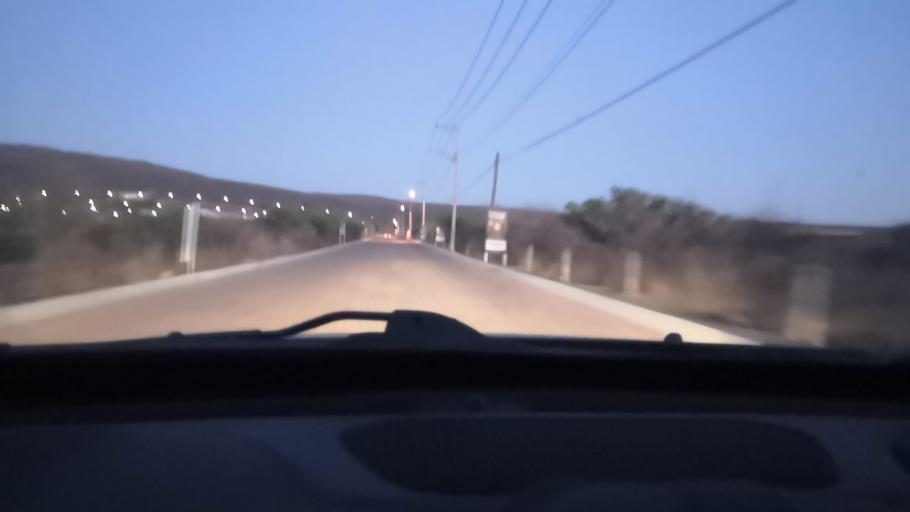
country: MX
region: Guanajuato
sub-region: Leon
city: Fraccionamiento Paseo de las Torres
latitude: 21.2355
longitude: -101.7881
